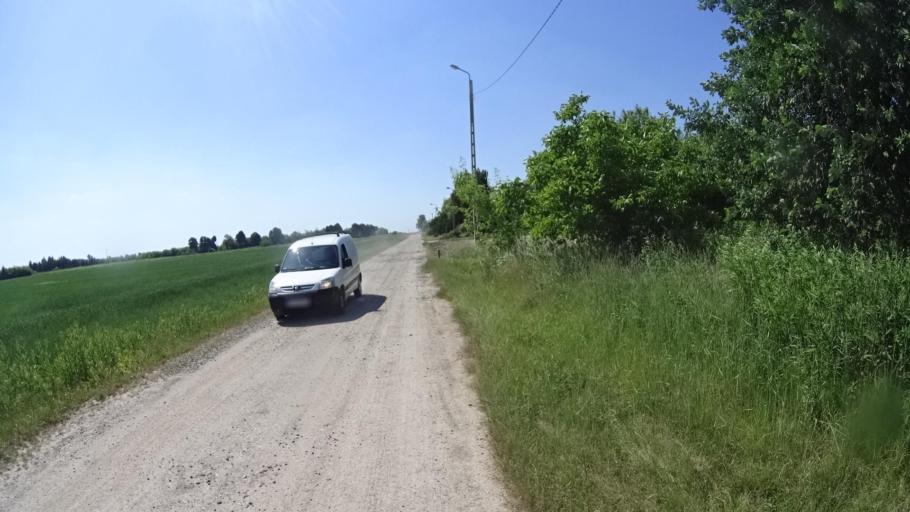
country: PL
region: Masovian Voivodeship
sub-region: Powiat warszawski zachodni
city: Jozefow
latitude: 52.2192
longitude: 20.6853
